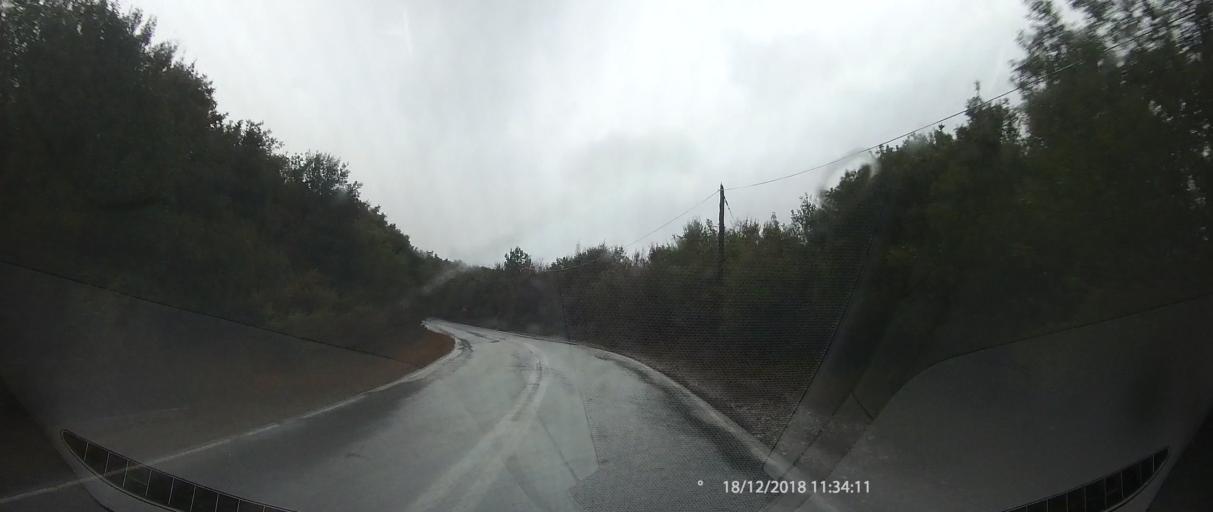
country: GR
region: Central Macedonia
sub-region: Nomos Pierias
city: Litochoro
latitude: 40.1147
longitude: 22.4900
